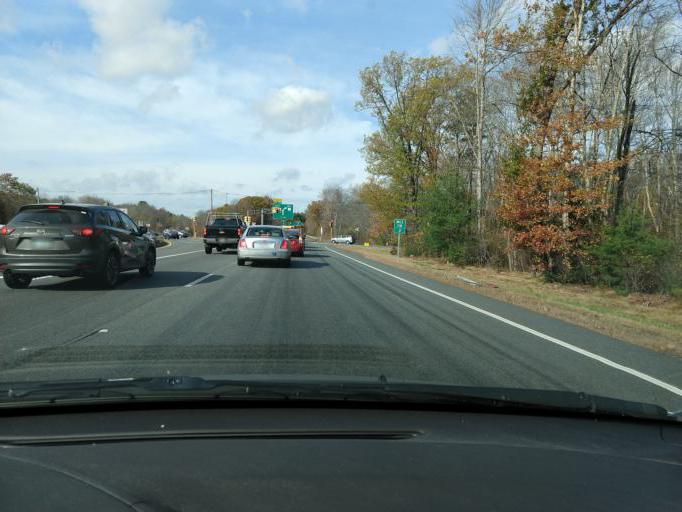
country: US
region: Massachusetts
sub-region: Middlesex County
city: Acton
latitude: 42.4728
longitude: -71.4395
